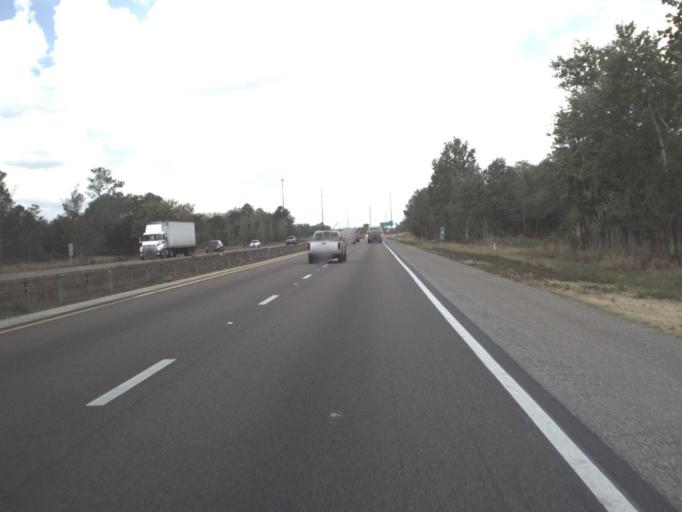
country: US
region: Florida
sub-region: Orange County
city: Wedgefield
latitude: 28.4517
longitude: -81.1497
